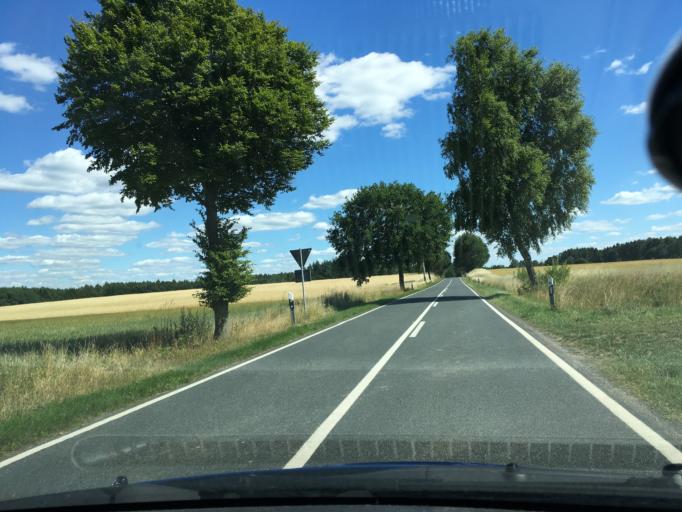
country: DE
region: Lower Saxony
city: Tosterglope
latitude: 53.2128
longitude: 10.8398
